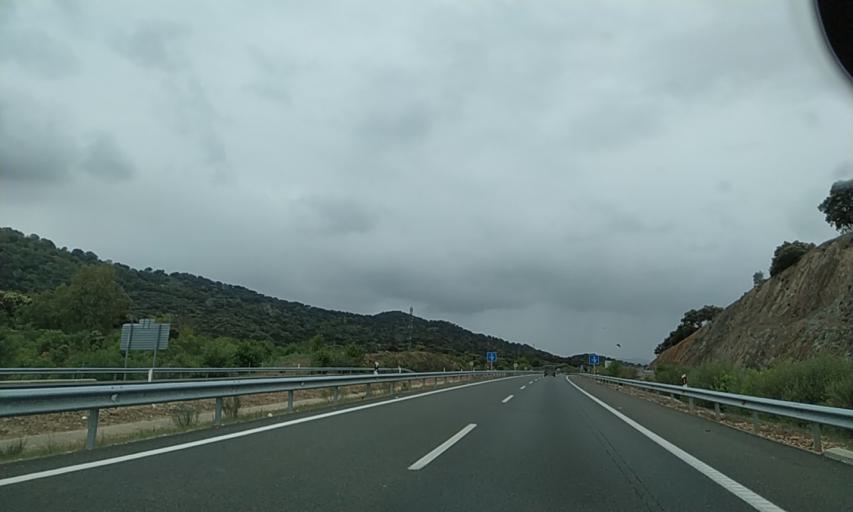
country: ES
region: Extremadura
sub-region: Provincia de Caceres
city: Oliva de Plasencia
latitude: 40.0904
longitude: -6.0729
